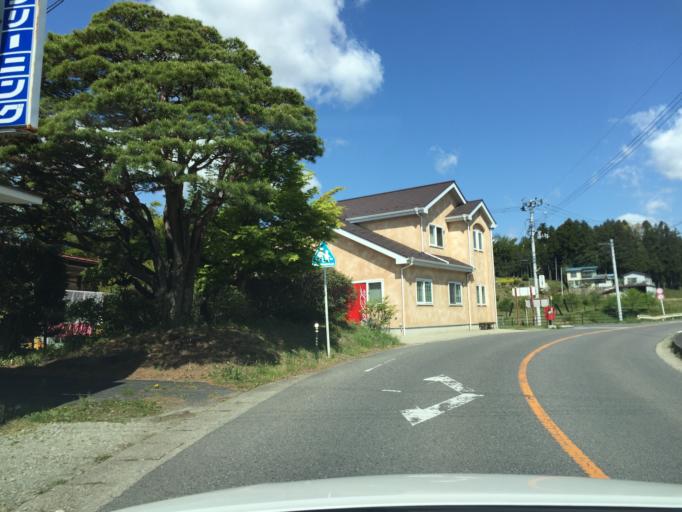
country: JP
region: Fukushima
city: Nihommatsu
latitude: 37.5723
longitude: 140.4692
